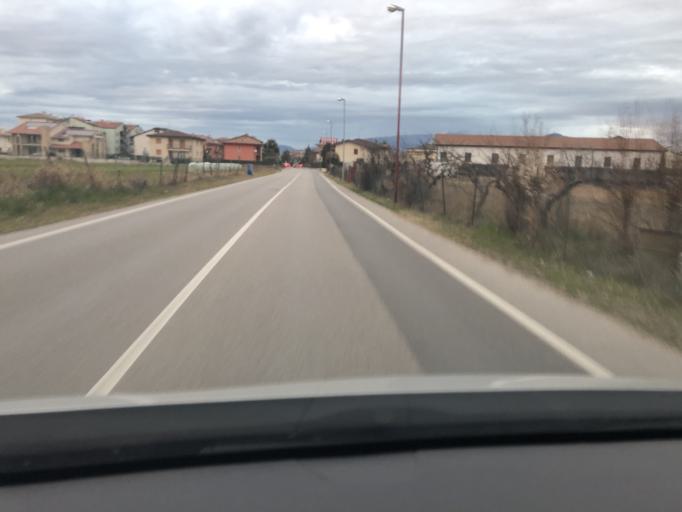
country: IT
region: Veneto
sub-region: Provincia di Verona
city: Bussolengo
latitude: 45.4602
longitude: 10.8565
